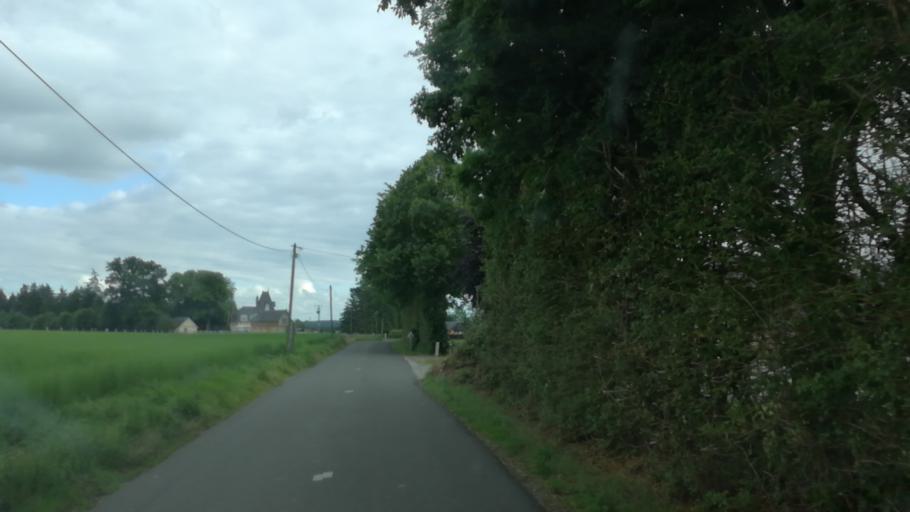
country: FR
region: Haute-Normandie
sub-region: Departement de l'Eure
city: Bourg-Achard
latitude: 49.2950
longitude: 0.8044
